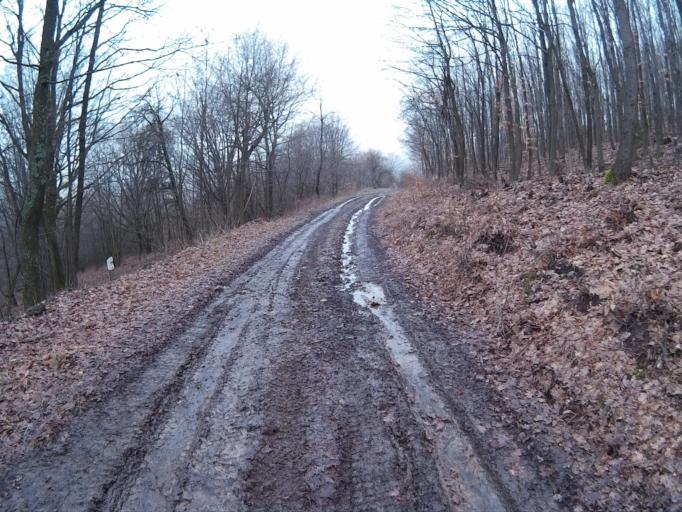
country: HU
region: Borsod-Abauj-Zemplen
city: Tolcsva
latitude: 48.3641
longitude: 21.4795
